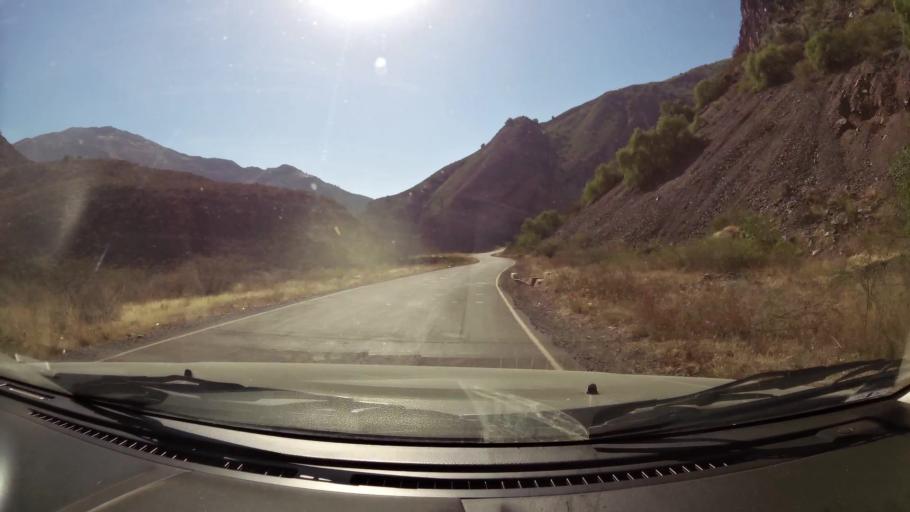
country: PE
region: Huancavelica
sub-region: Provincia de Acobamba
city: Pomacocha
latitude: -12.7916
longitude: -74.4874
